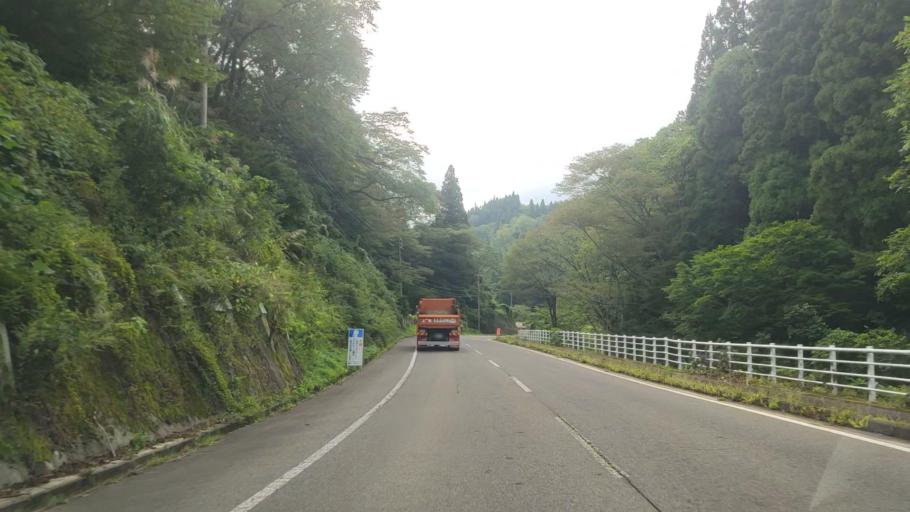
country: JP
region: Nagano
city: Iiyama
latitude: 36.9065
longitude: 138.3145
